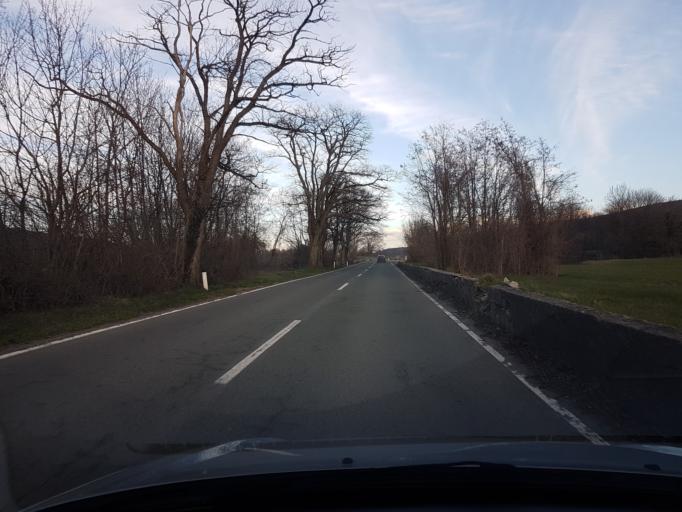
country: SI
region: Hrpelje-Kozina
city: Kozina
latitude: 45.6611
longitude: 13.9086
